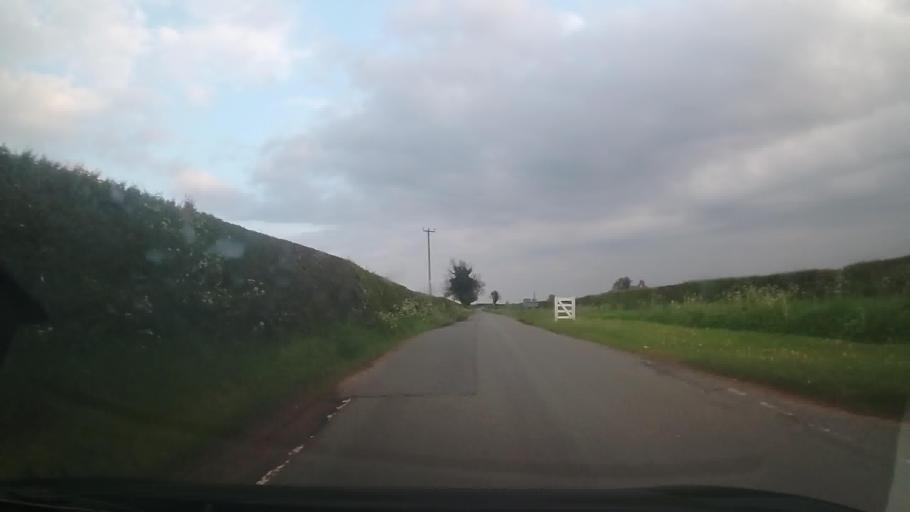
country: GB
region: England
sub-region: Shropshire
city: Ellesmere
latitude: 52.9122
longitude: -2.8046
